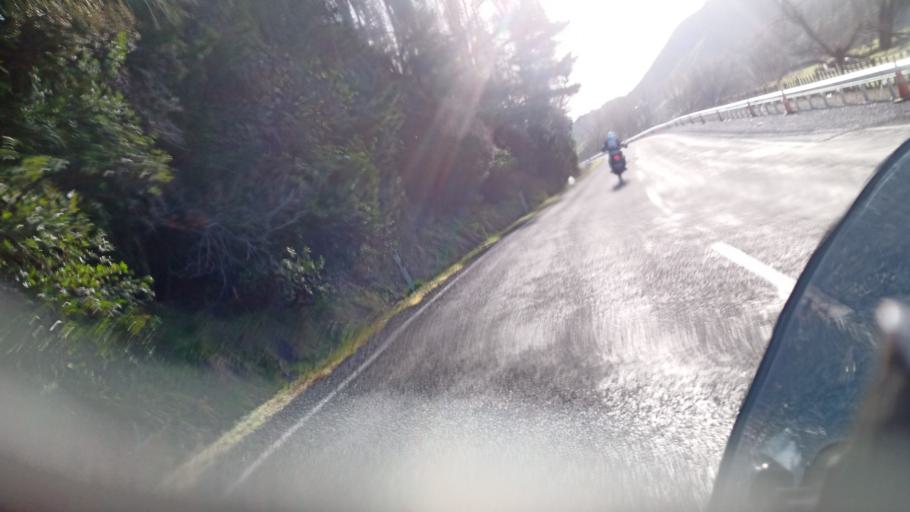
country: NZ
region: Gisborne
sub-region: Gisborne District
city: Gisborne
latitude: -38.4383
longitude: 177.5788
